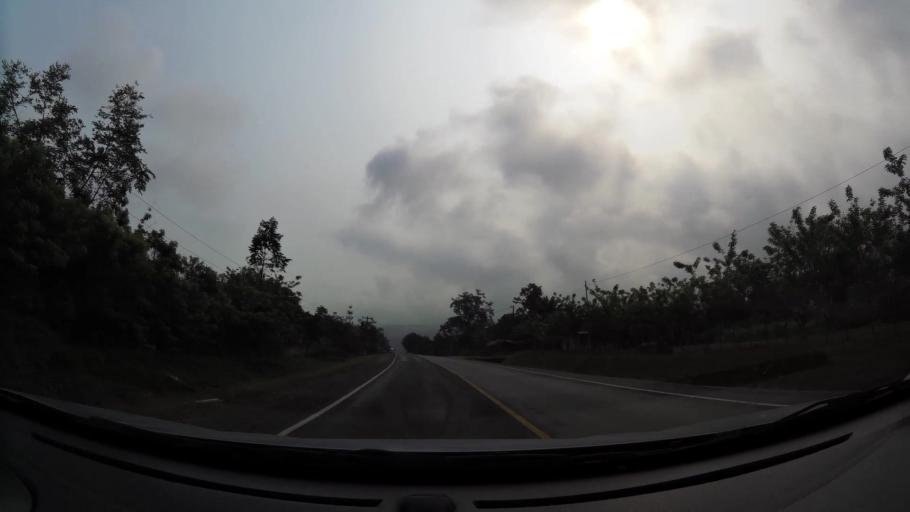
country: HN
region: Yoro
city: Toyos
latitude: 15.5559
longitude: -87.6275
